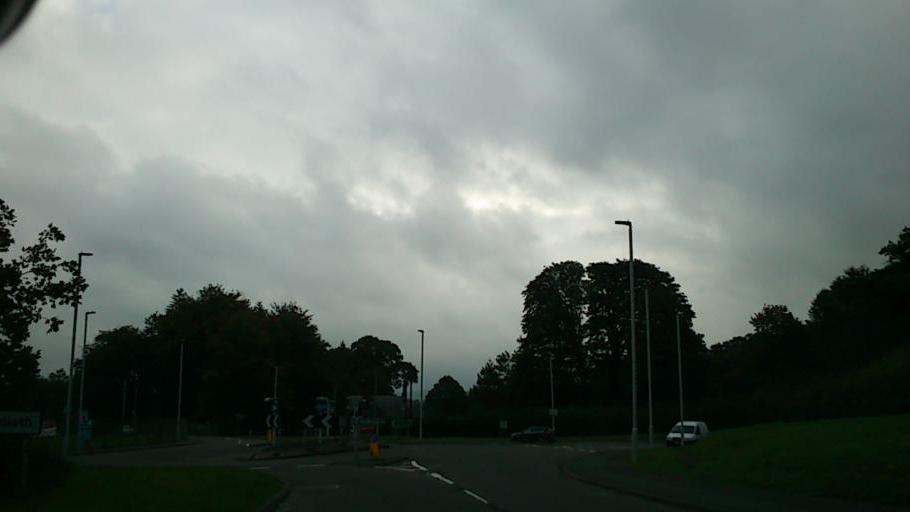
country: GB
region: Wales
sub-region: Sir Powys
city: Machynlleth
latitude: 52.5867
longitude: -3.8579
